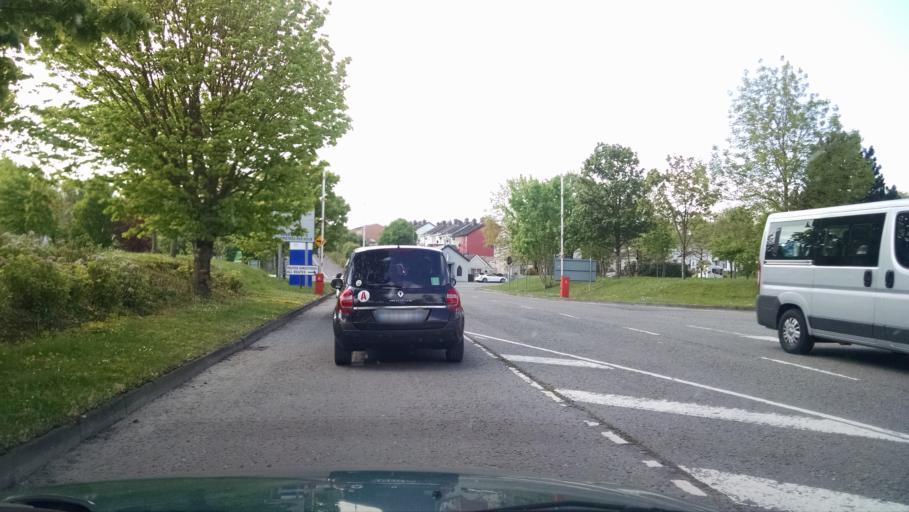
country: IE
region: Munster
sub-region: County Cork
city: Cobh
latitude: 51.8312
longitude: -8.3158
